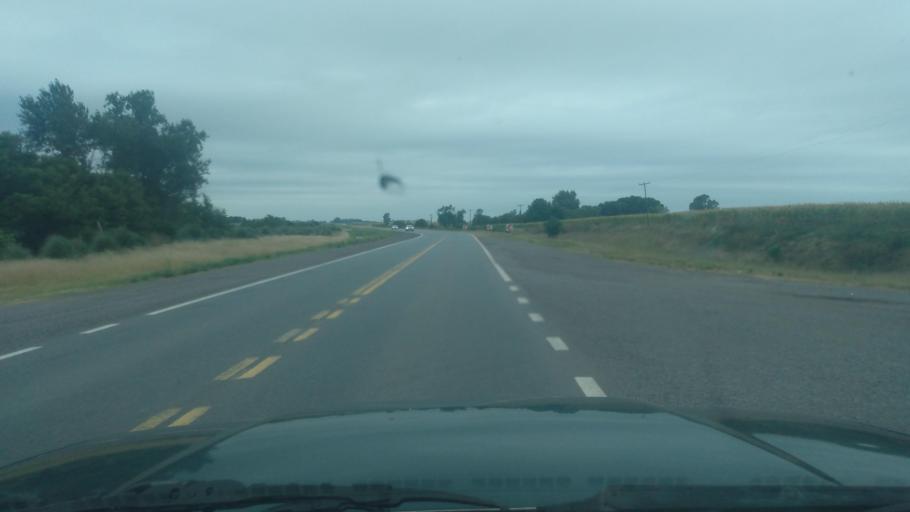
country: AR
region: Buenos Aires
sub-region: Partido de Bragado
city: Bragado
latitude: -35.3231
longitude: -60.6409
